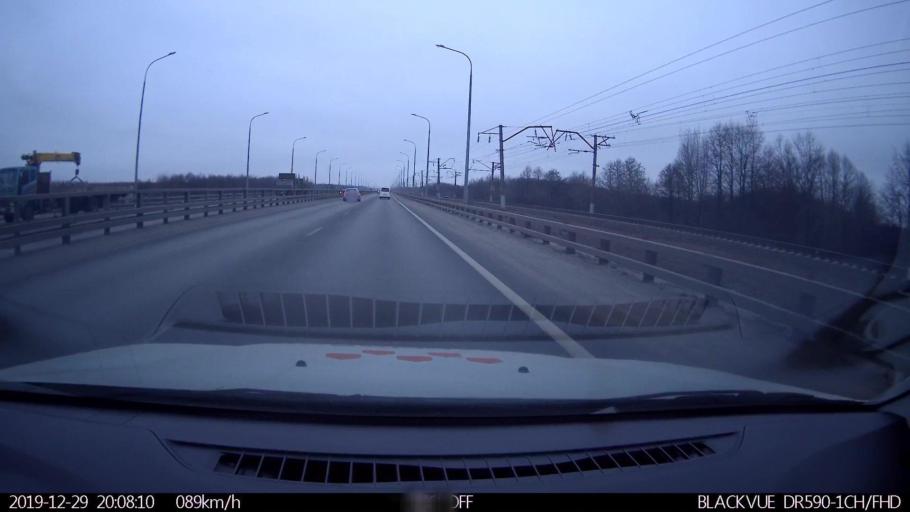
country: RU
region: Nizjnij Novgorod
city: Neklyudovo
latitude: 56.3881
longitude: 43.9700
